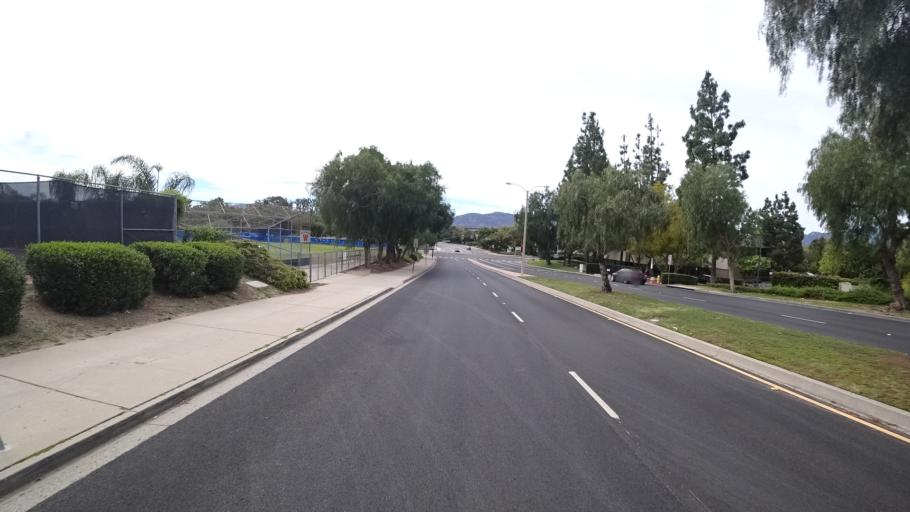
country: US
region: California
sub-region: Los Angeles County
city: Westlake Village
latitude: 34.1599
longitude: -118.8177
